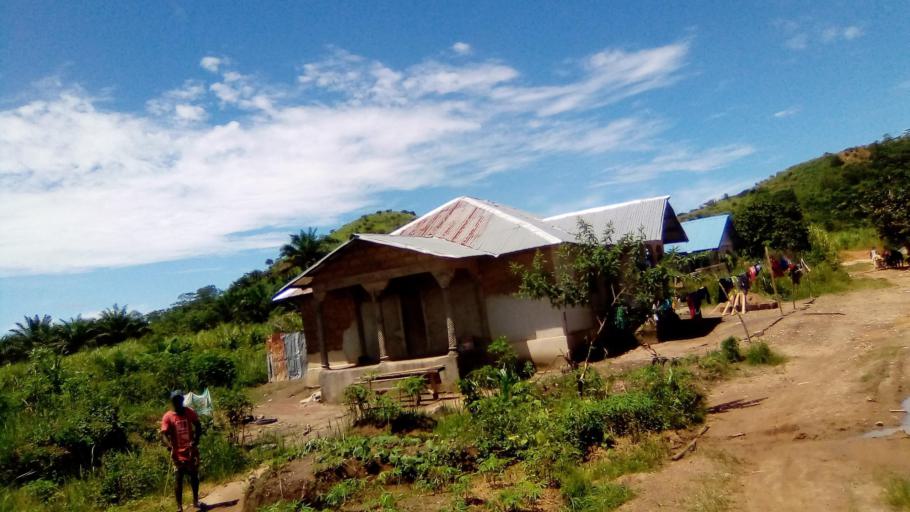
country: SL
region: Eastern Province
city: Simbakoro
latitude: 8.6218
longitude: -11.0006
